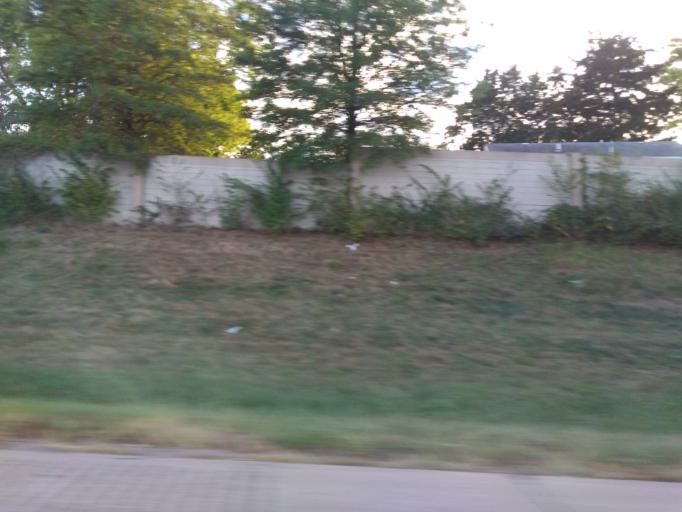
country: US
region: Missouri
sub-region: Saint Louis County
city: Sappington
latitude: 38.5208
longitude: -90.3933
